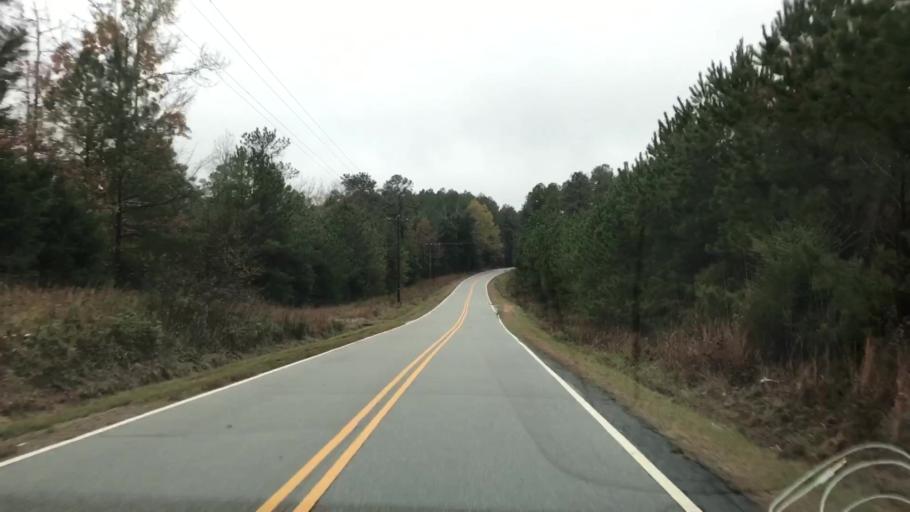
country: US
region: South Carolina
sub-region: Greenwood County
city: Ninety Six
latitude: 34.3075
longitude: -81.9598
